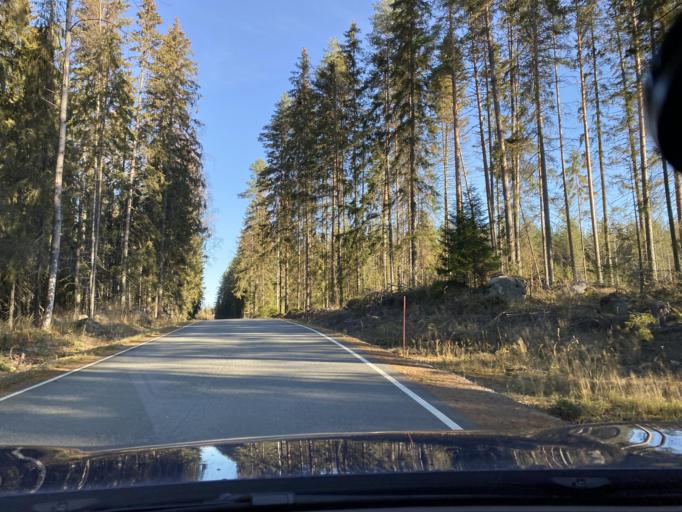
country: FI
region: Haeme
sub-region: Haemeenlinna
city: Kalvola
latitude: 61.0280
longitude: 24.1870
